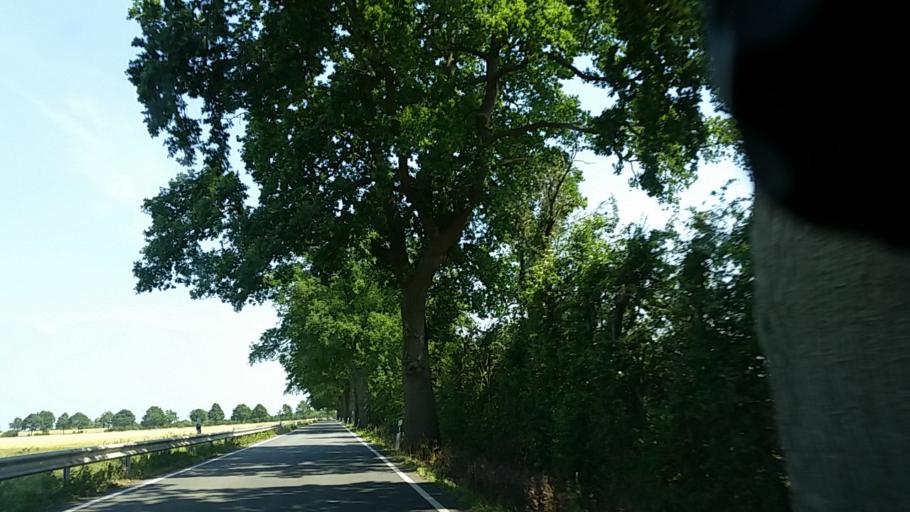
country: DE
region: Lower Saxony
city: Thedinghausen
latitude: 52.9848
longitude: 9.0006
